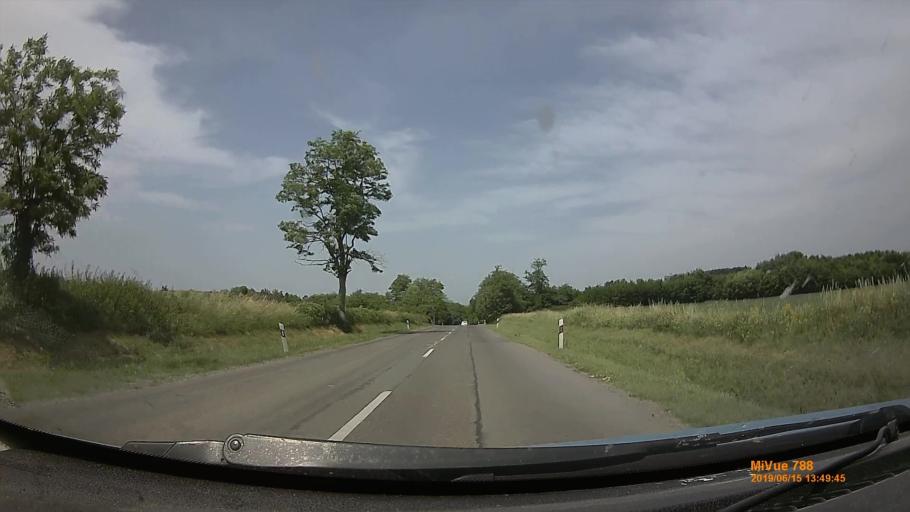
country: HU
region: Tolna
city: Iregszemcse
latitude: 46.7339
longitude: 18.1658
